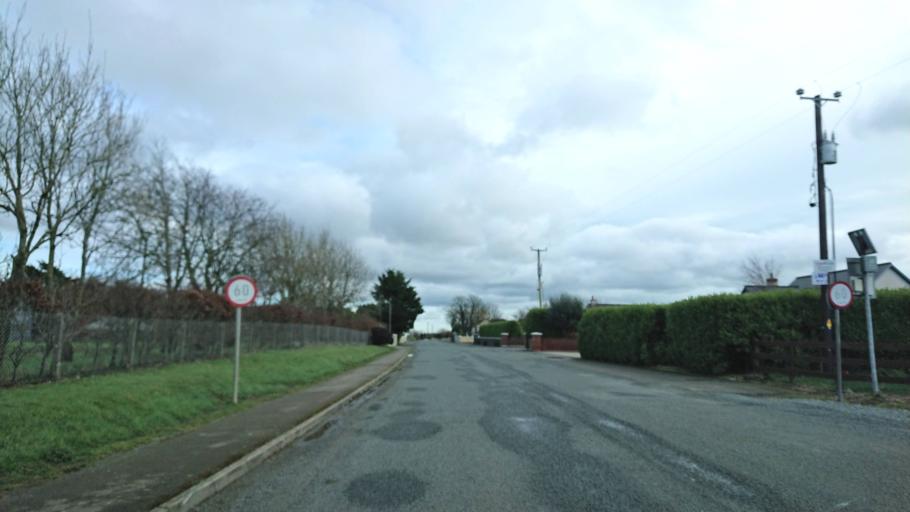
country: IE
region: Munster
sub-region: Waterford
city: Dunmore East
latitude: 52.2448
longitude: -6.9148
